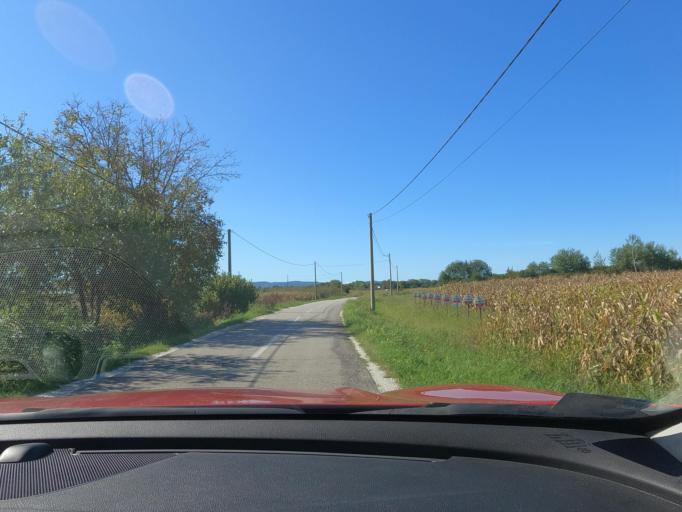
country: HR
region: Sisacko-Moslavacka
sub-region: Grad Sisak
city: Sisak
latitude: 45.4856
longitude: 16.3339
